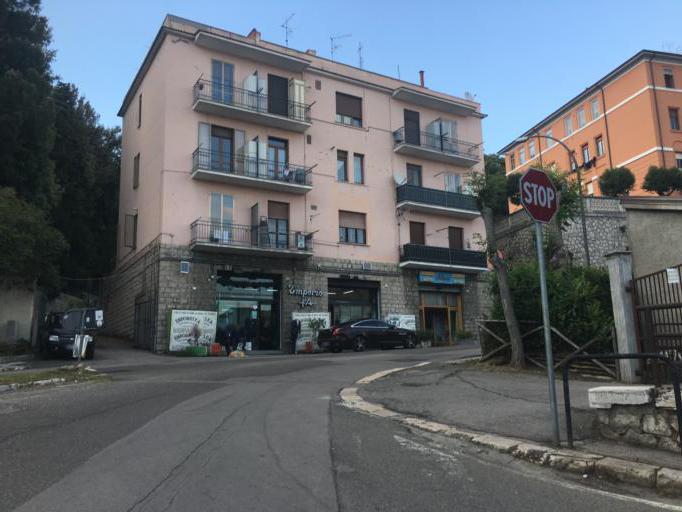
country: IT
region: Basilicate
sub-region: Provincia di Potenza
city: Potenza
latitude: 40.6354
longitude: 15.8041
